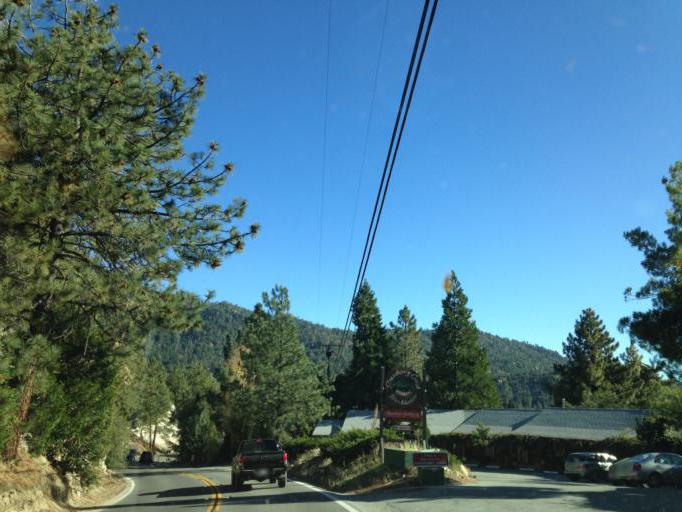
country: US
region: California
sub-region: Riverside County
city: Idyllwild-Pine Cove
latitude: 33.7517
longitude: -116.7184
